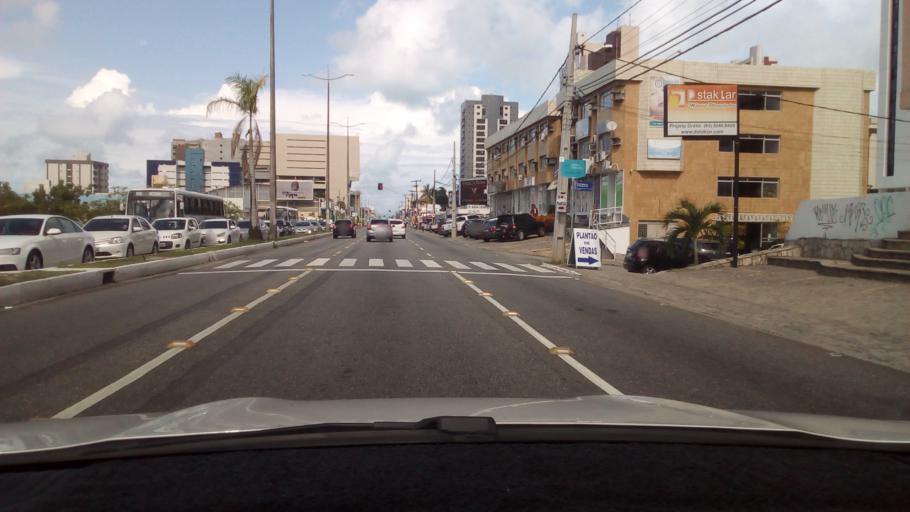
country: BR
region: Paraiba
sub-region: Joao Pessoa
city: Joao Pessoa
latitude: -7.0977
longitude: -34.8412
